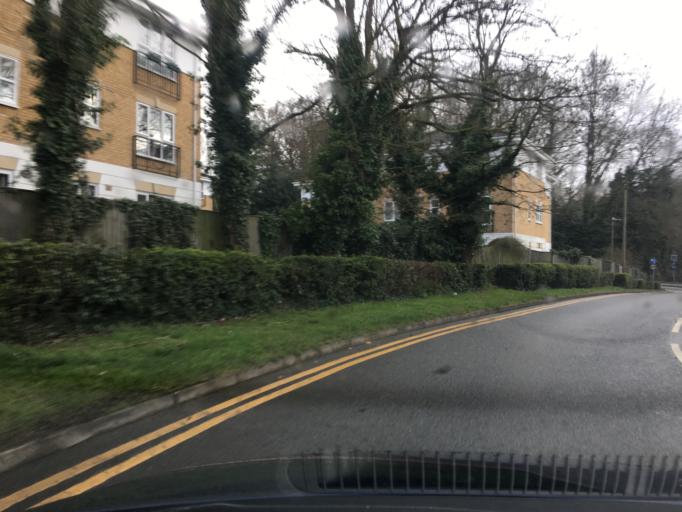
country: GB
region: England
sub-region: Bracknell Forest
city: Bracknell
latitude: 51.4118
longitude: -0.7551
